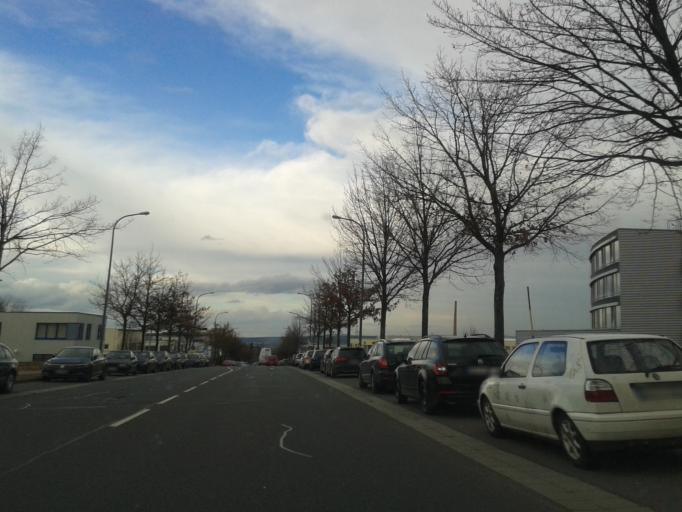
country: DE
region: Saxony
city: Bannewitz
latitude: 51.0072
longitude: 13.6987
